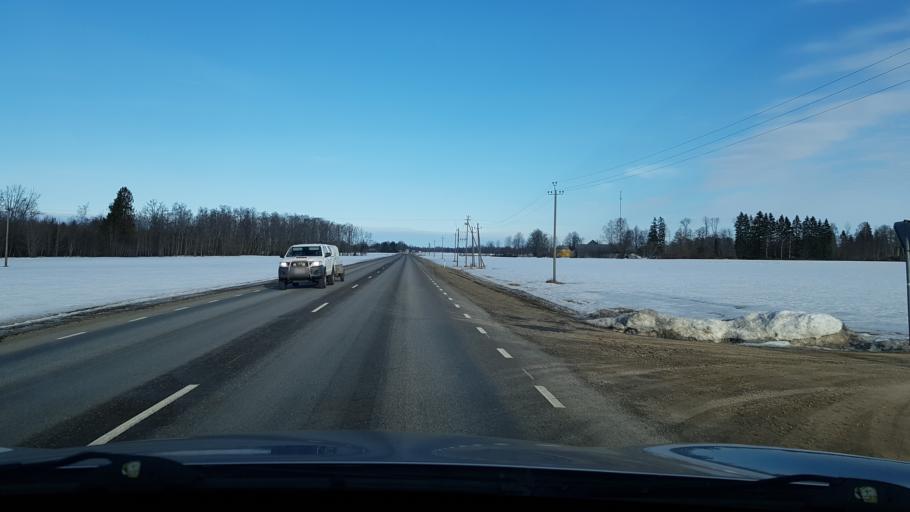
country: EE
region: Viljandimaa
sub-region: Viljandi linn
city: Viljandi
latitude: 58.4512
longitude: 25.5952
